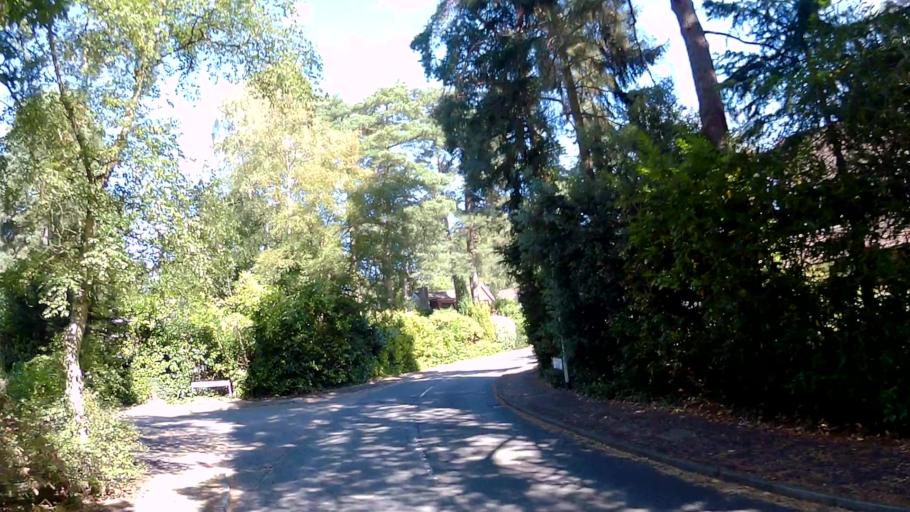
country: GB
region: England
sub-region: Bracknell Forest
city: Crowthorne
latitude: 51.3727
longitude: -0.8081
